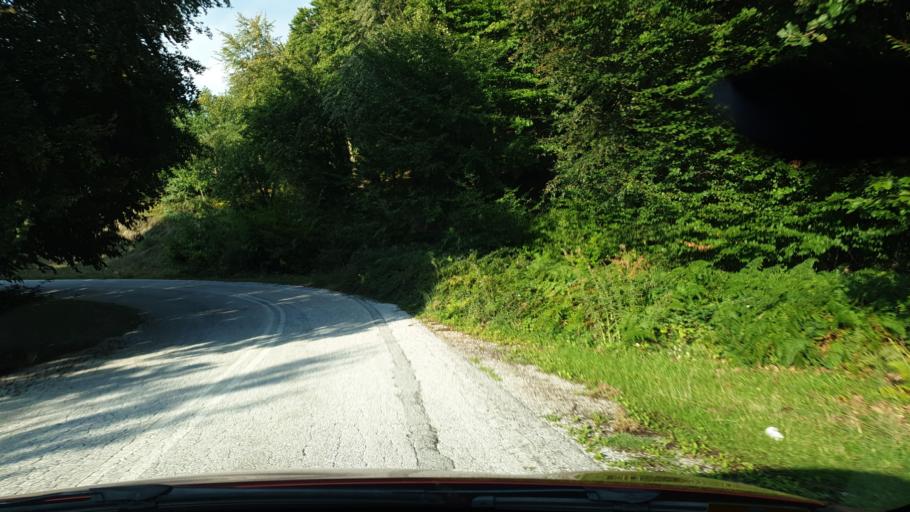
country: GR
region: Central Macedonia
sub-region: Nomos Chalkidikis
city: Galatista
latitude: 40.5064
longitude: 23.2423
